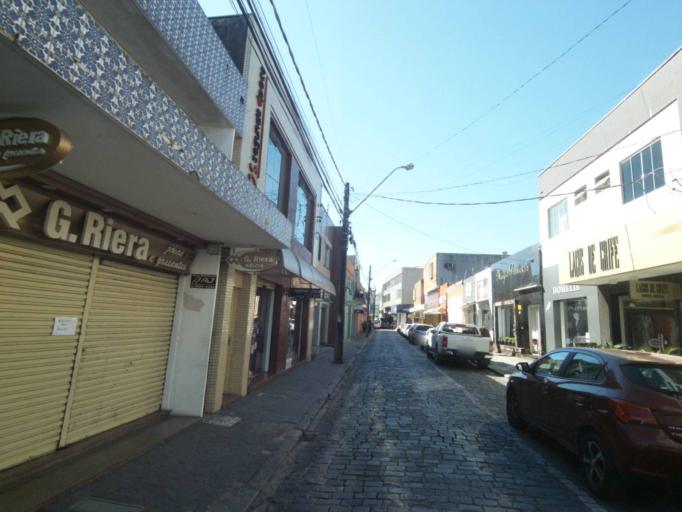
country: BR
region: Parana
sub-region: Paranagua
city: Paranagua
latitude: -25.5205
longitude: -48.5071
